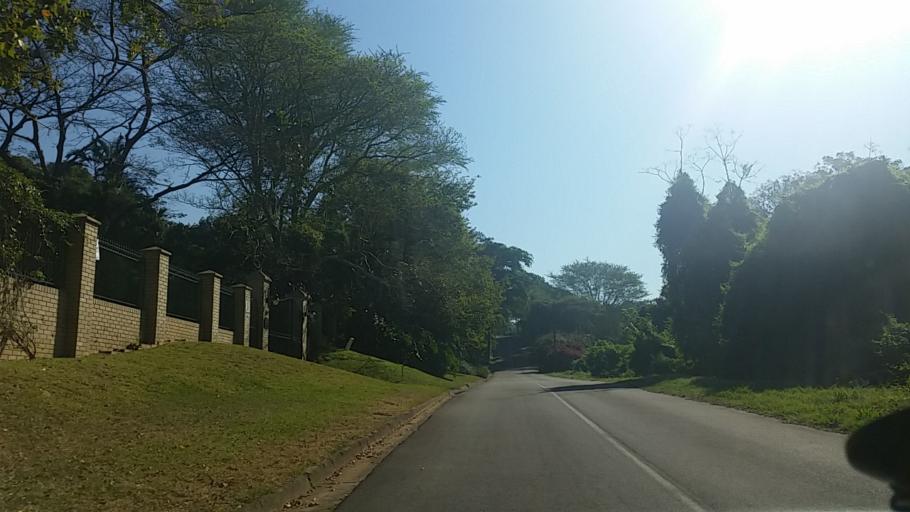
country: ZA
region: KwaZulu-Natal
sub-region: eThekwini Metropolitan Municipality
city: Berea
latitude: -29.8549
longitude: 30.9068
